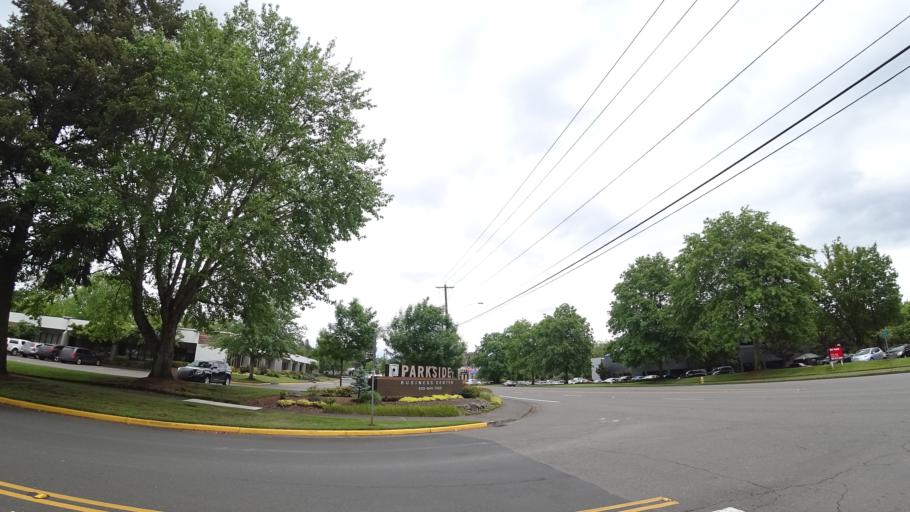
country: US
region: Oregon
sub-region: Washington County
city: Beaverton
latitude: 45.4601
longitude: -122.7912
